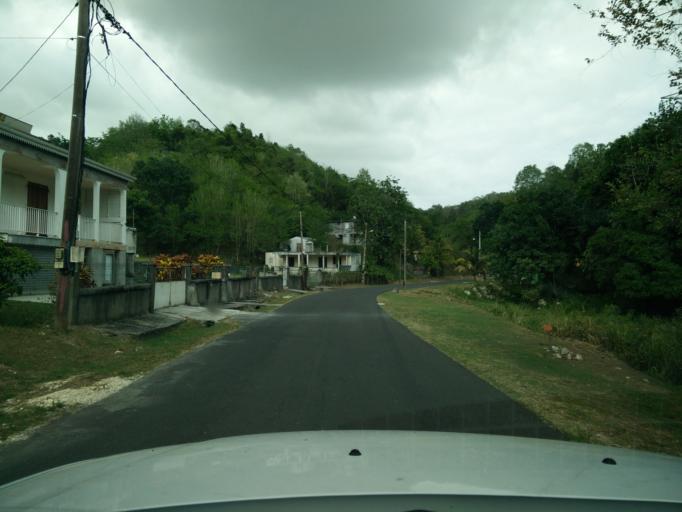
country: GP
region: Guadeloupe
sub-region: Guadeloupe
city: Le Gosier
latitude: 16.2237
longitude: -61.4675
